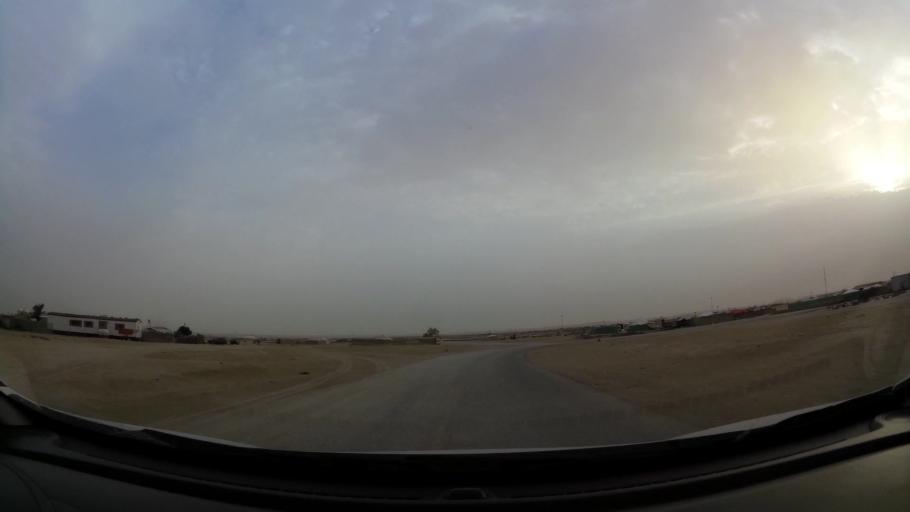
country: BH
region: Central Governorate
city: Dar Kulayb
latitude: 25.9994
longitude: 50.5851
